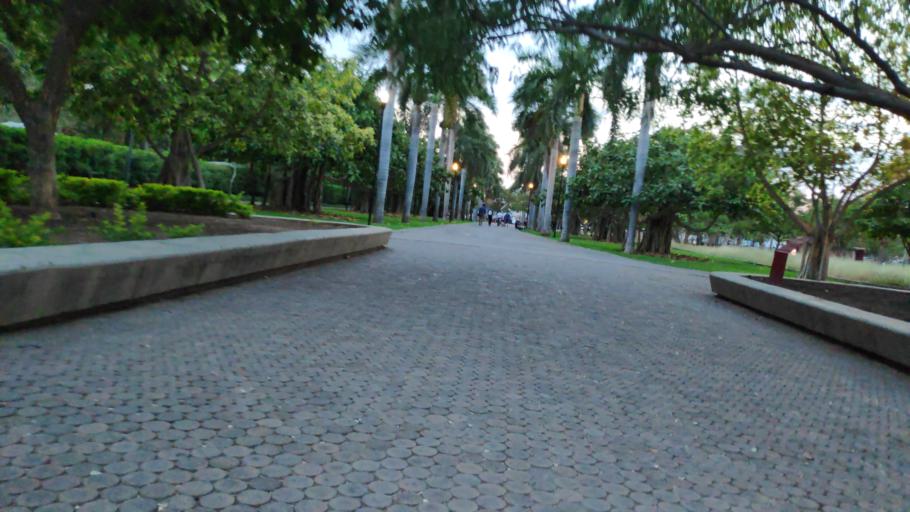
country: MX
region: Sinaloa
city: Culiacan
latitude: 24.8241
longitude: -107.3860
